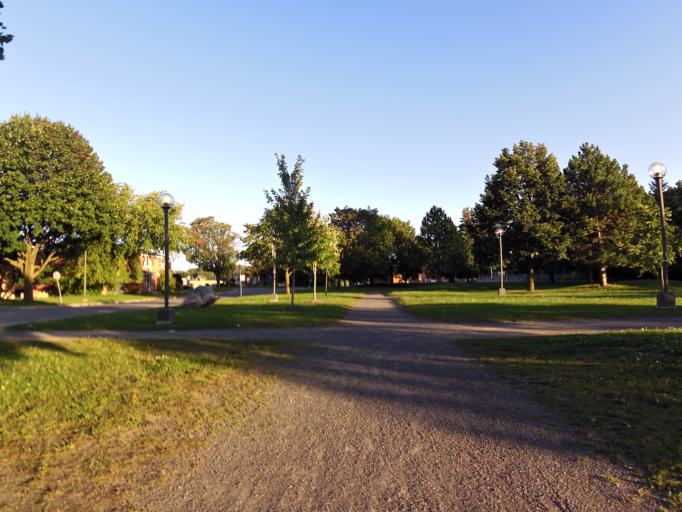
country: CA
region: Quebec
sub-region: Outaouais
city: Gatineau
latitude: 45.4447
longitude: -75.7171
